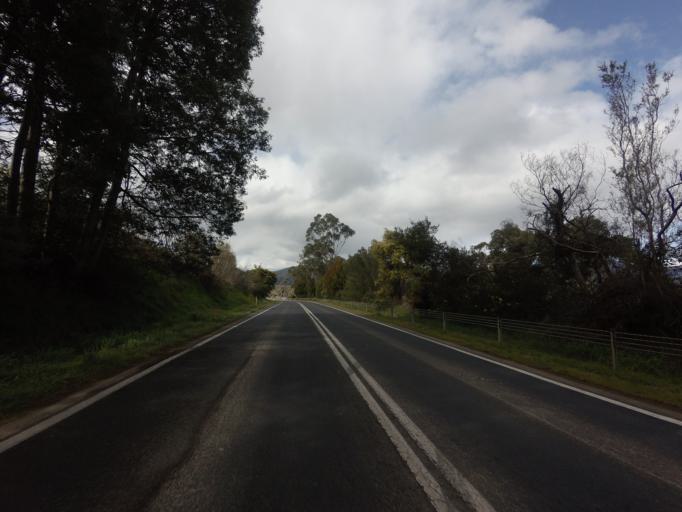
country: AU
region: Tasmania
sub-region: Huon Valley
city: Franklin
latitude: -43.0702
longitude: 147.0224
